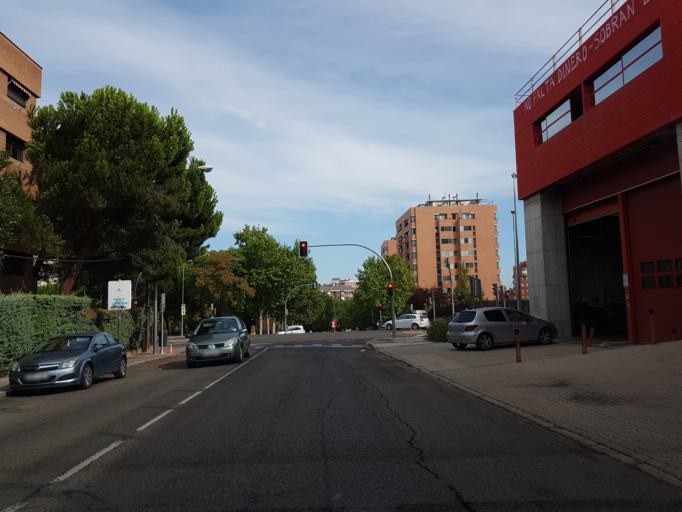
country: ES
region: Madrid
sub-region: Provincia de Madrid
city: Pinar de Chamartin
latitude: 40.4744
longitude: -3.6653
